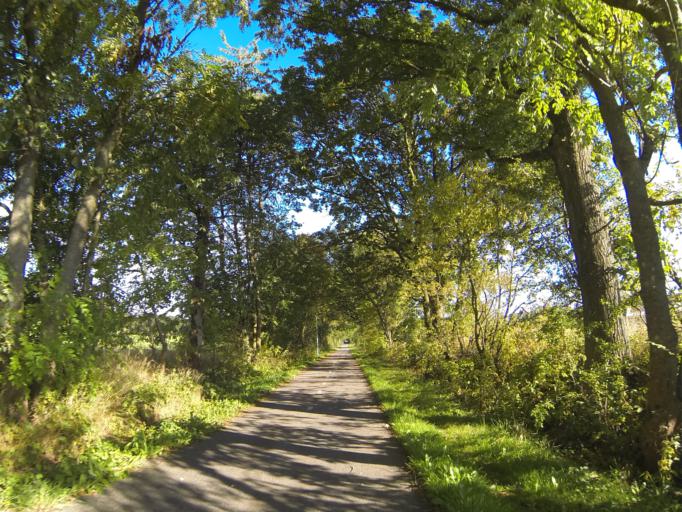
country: SE
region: Skane
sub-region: Lunds Kommun
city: Lund
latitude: 55.7133
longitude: 13.3147
